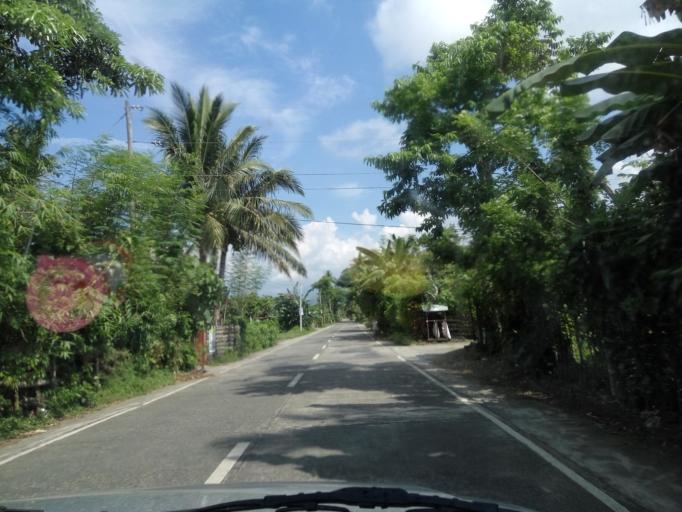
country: PH
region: Central Luzon
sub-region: Province of Aurora
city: Suklayin
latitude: 15.7972
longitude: 121.5429
